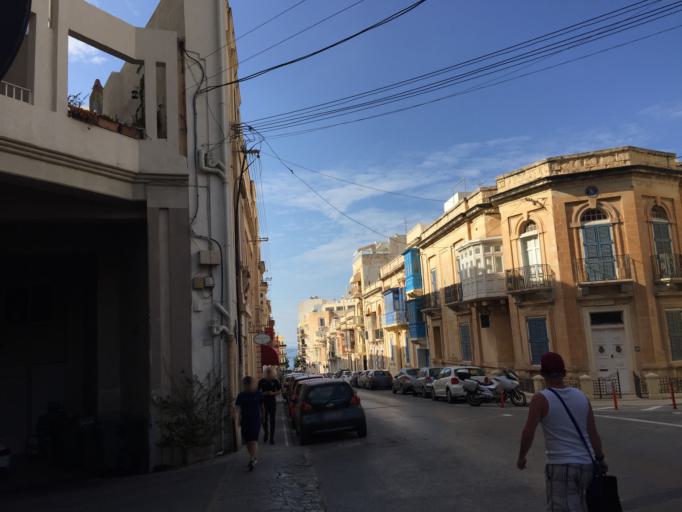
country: MT
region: Tas-Sliema
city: Sliema
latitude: 35.9127
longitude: 14.5047
